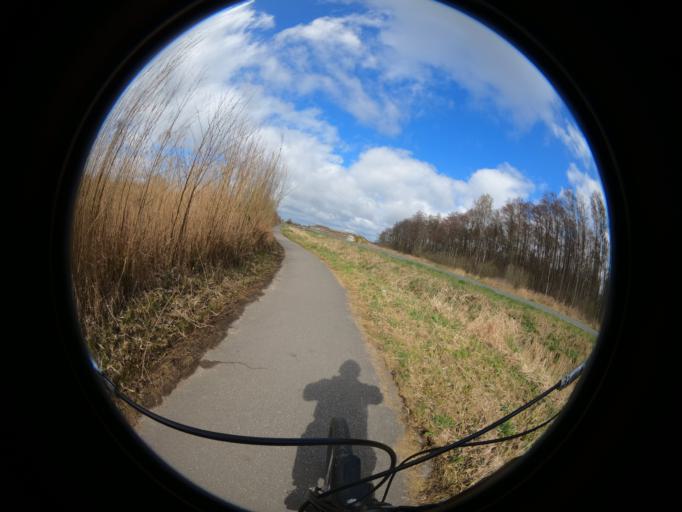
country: DE
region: Lower Saxony
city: Neu Wulmstorf
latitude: 53.4842
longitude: 9.7820
